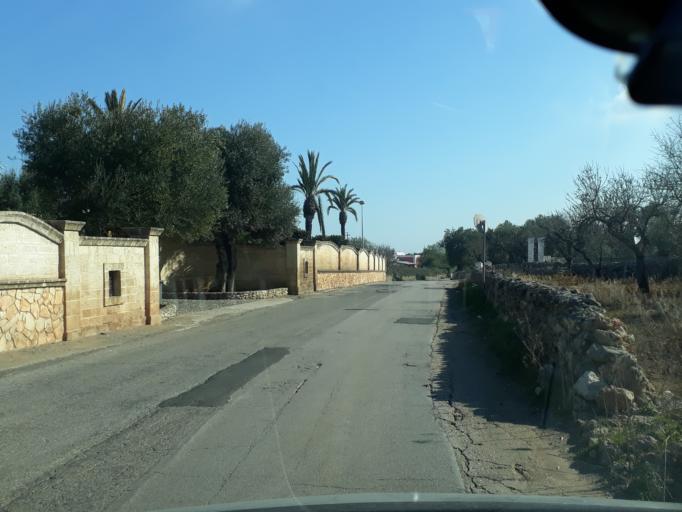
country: IT
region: Apulia
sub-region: Provincia di Brindisi
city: Fasano
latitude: 40.8259
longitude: 17.3787
